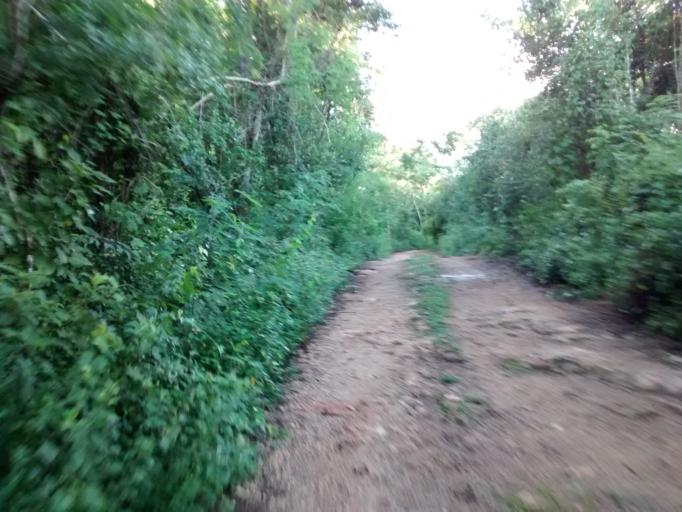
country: MX
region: Yucatan
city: Valladolid
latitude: 20.7130
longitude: -88.2068
